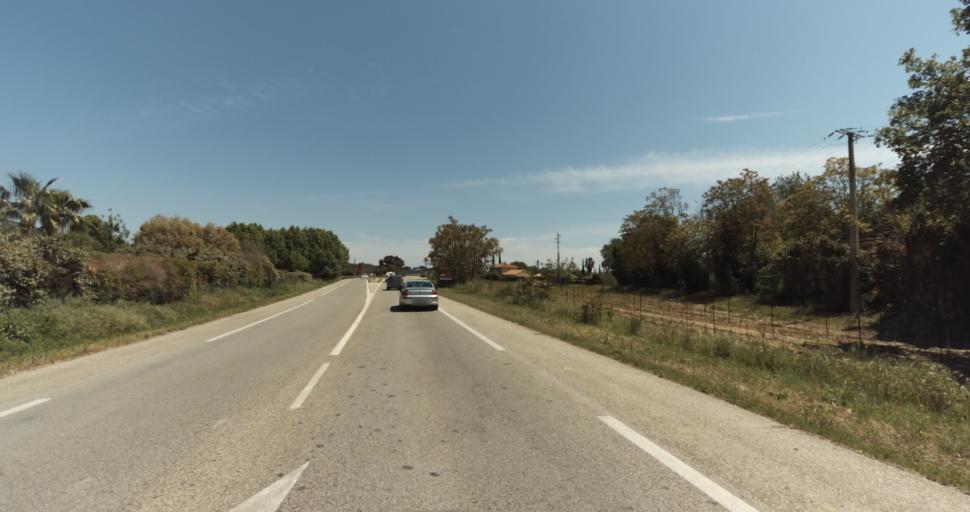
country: FR
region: Provence-Alpes-Cote d'Azur
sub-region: Departement du Var
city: Hyeres
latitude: 43.1454
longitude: 6.1511
